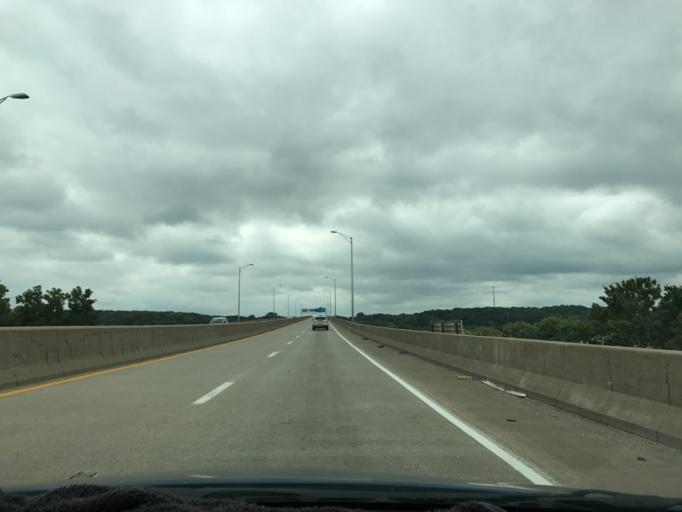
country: US
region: Iowa
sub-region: Scott County
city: Le Claire
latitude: 41.5845
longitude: -90.3677
